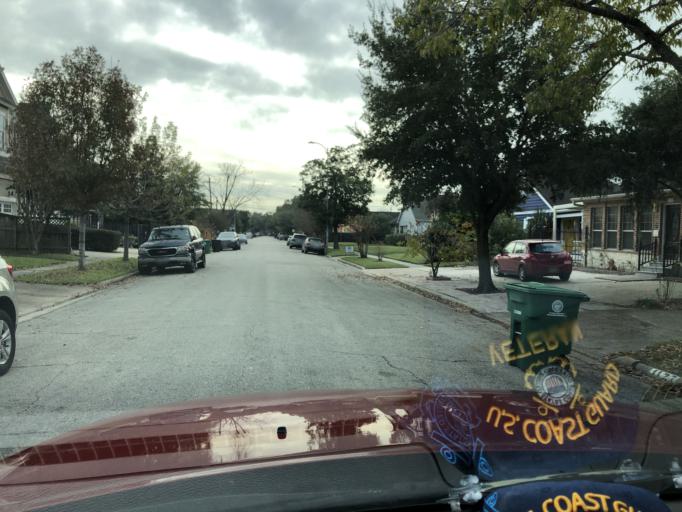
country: US
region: Texas
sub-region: Harris County
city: Houston
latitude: 29.7916
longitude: -95.4089
